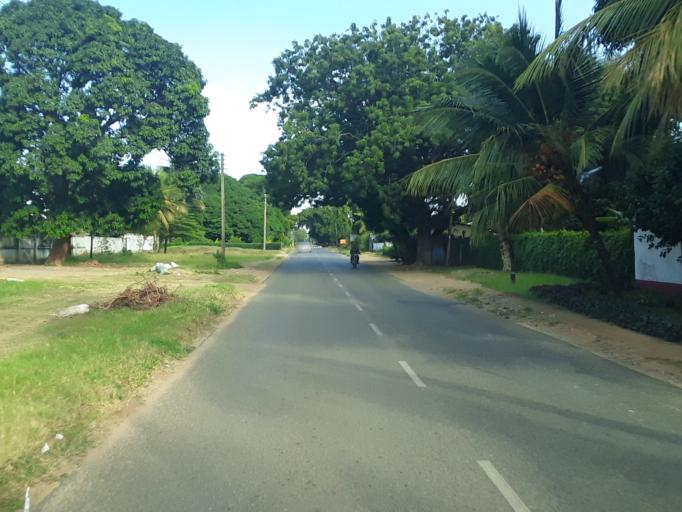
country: TZ
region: Tanga
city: Tanga
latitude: -5.0728
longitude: 39.1137
